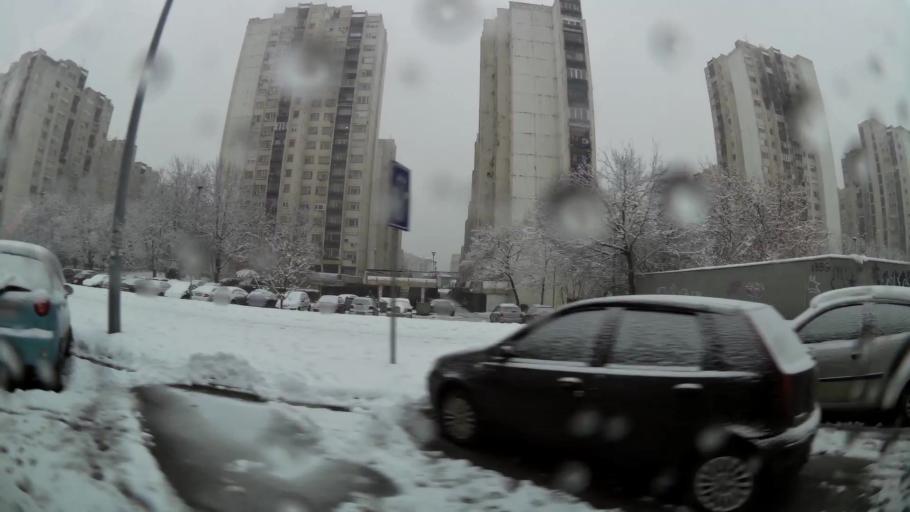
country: RS
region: Central Serbia
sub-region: Belgrade
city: Novi Beograd
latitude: 44.8062
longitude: 20.3836
